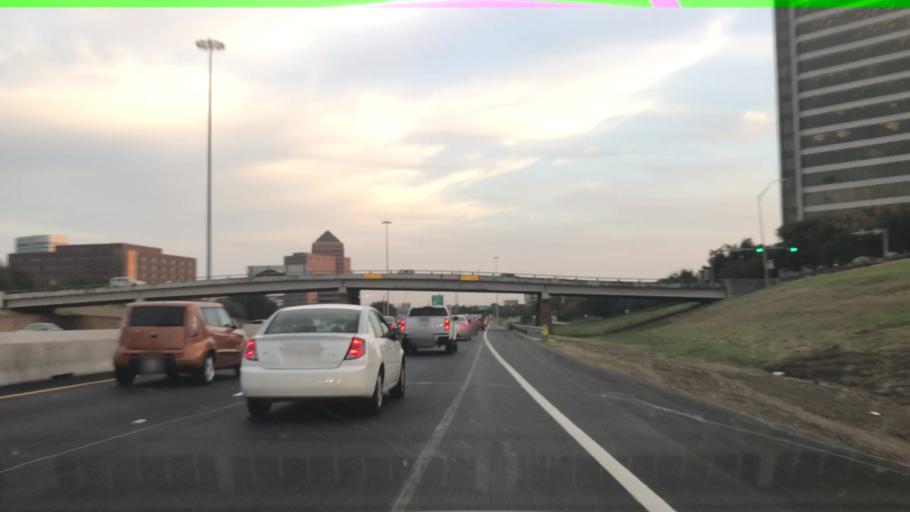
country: US
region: Texas
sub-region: Dallas County
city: Irving
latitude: 32.8643
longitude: -96.9401
